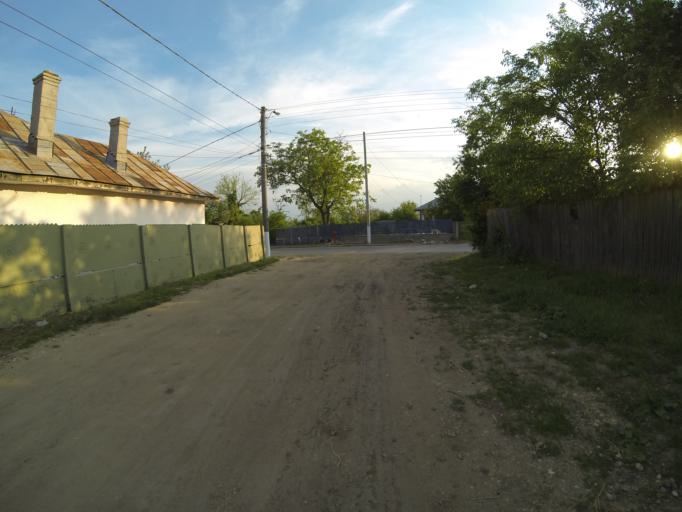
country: RO
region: Dolj
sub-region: Comuna Segarcea
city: Segarcea
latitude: 44.0964
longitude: 23.7505
